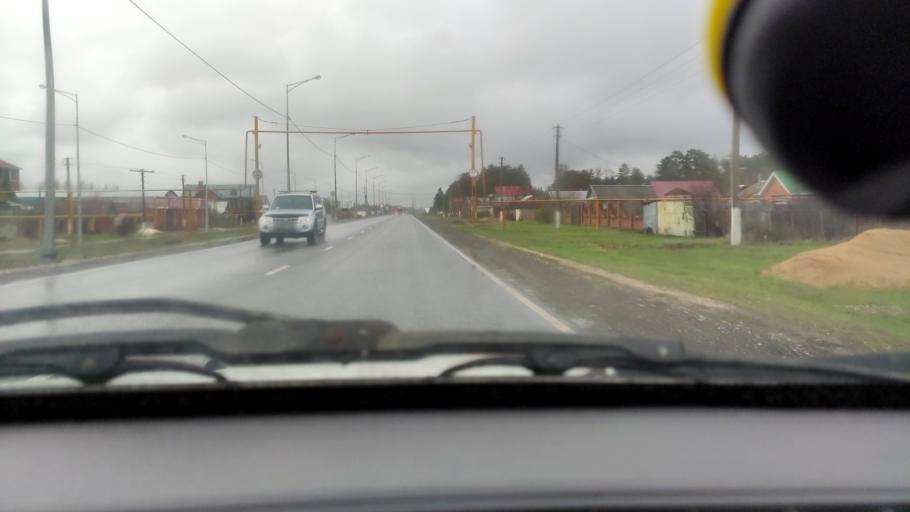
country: RU
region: Samara
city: Povolzhskiy
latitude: 53.5889
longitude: 49.5767
